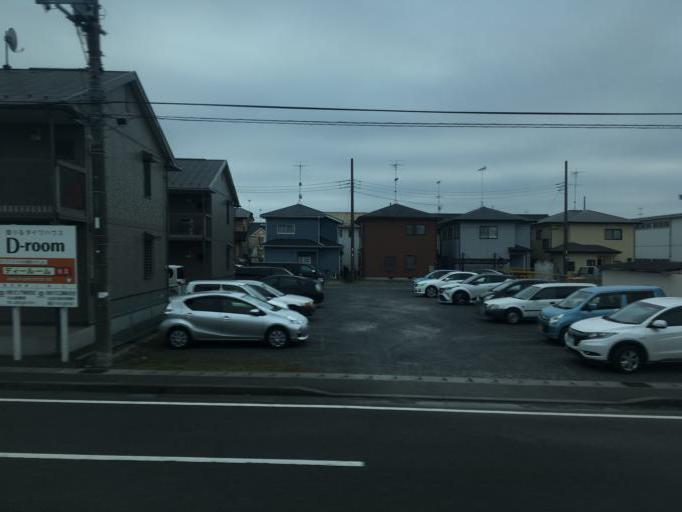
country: JP
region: Tochigi
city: Oyama
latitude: 36.3044
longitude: 139.8273
